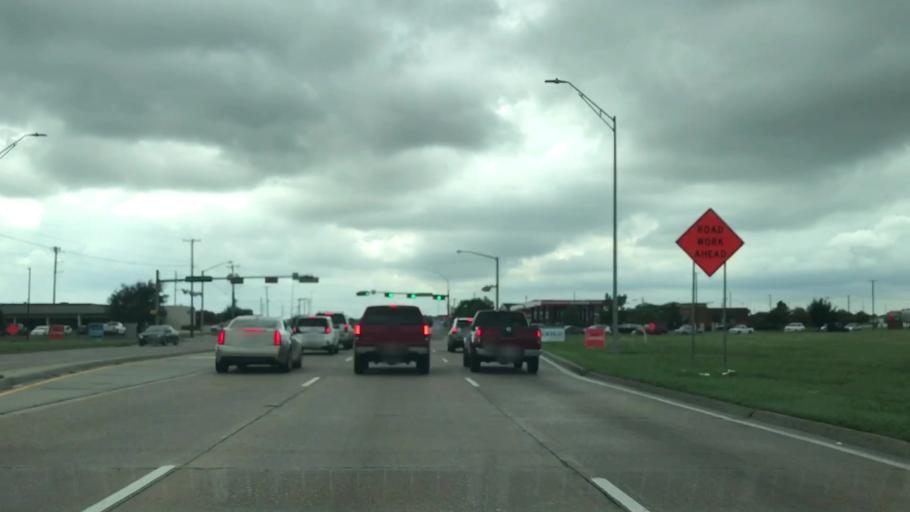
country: US
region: Texas
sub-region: Dallas County
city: Garland
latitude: 32.9108
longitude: -96.6107
